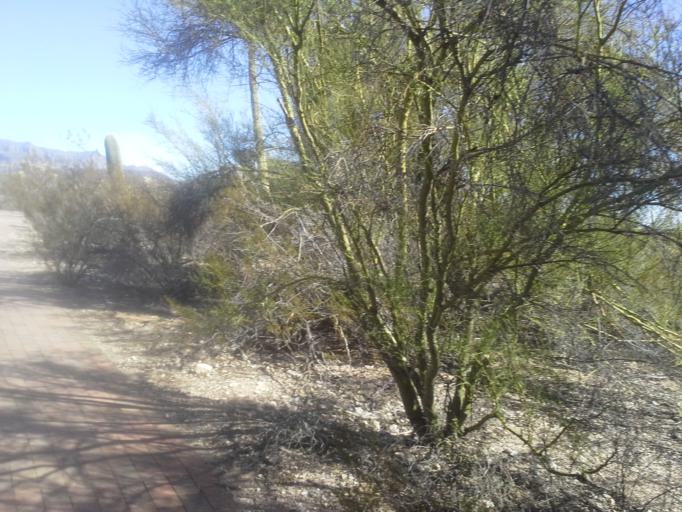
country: MX
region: Sonora
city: Sonoyta
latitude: 31.9549
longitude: -112.8008
